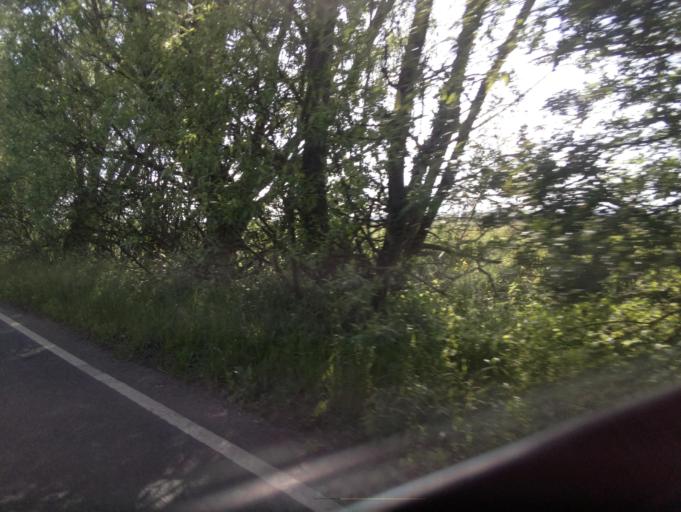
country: GB
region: England
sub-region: Somerset
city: Westonzoyland
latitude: 51.0639
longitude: -2.9283
